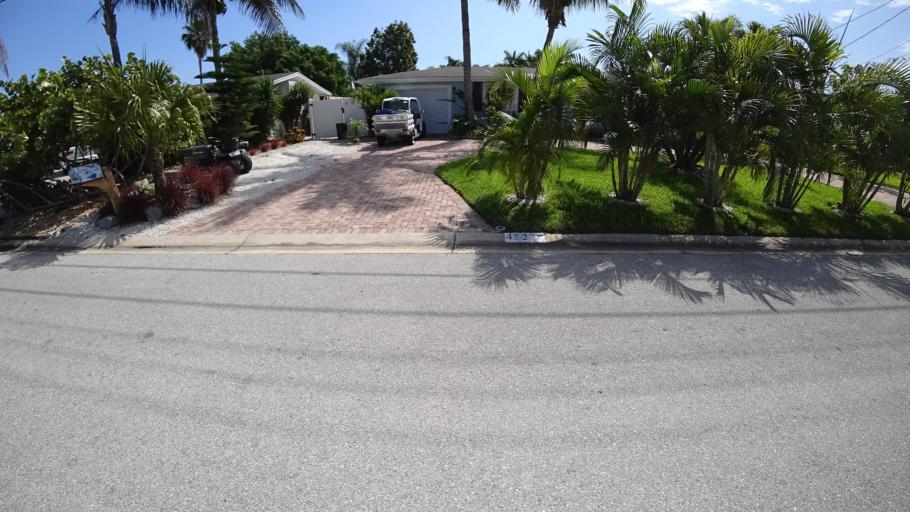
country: US
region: Florida
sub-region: Manatee County
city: Cortez
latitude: 27.4587
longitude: -82.6549
